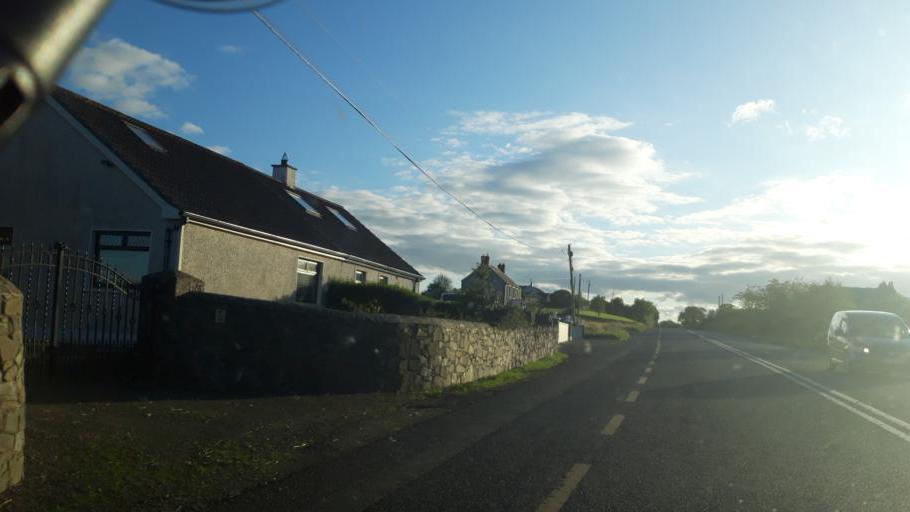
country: IE
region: Leinster
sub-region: Lu
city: Carlingford
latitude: 54.0162
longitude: -6.1549
